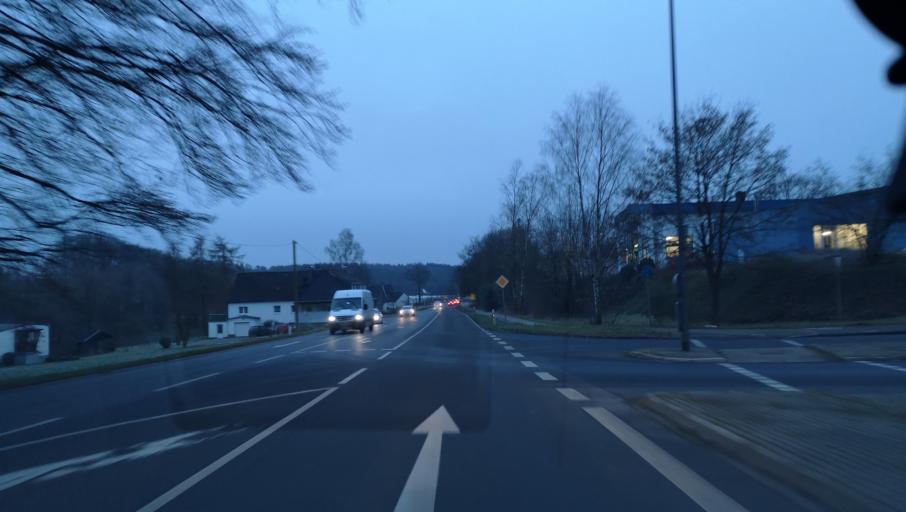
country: DE
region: North Rhine-Westphalia
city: Radevormwald
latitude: 51.2045
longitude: 7.3894
